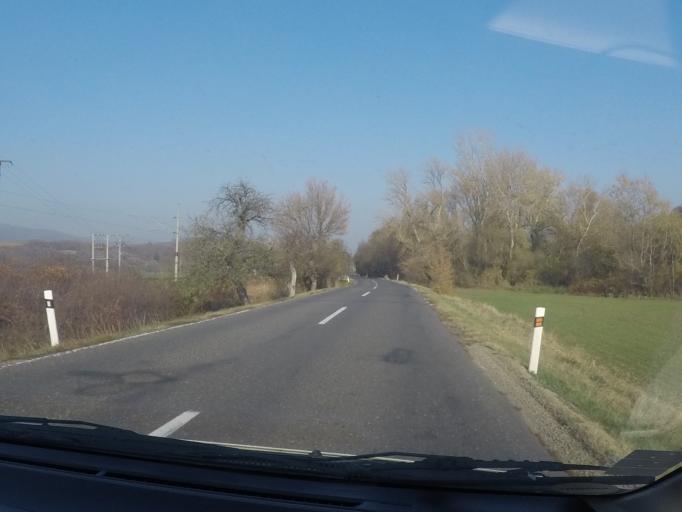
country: SK
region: Nitriansky
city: Tlmace
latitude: 48.3210
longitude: 18.5411
